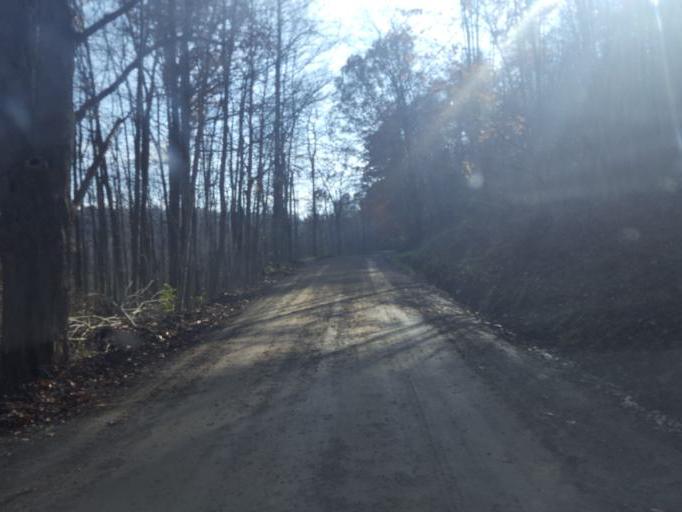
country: US
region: Ohio
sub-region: Knox County
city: Oak Hill
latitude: 40.4069
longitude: -82.2206
